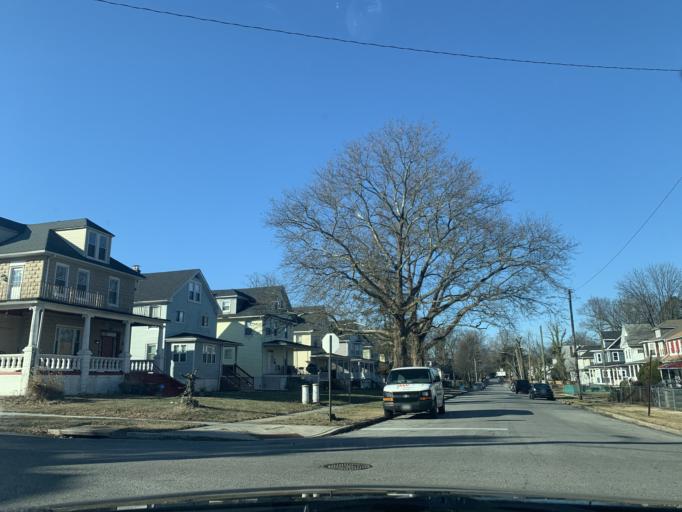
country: US
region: Maryland
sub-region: Baltimore County
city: Lochearn
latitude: 39.3377
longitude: -76.6893
